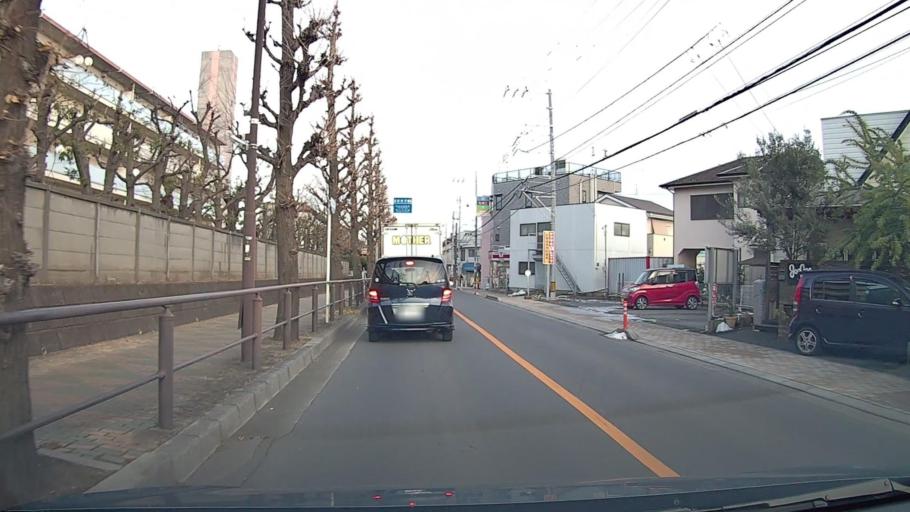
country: JP
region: Saitama
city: Wako
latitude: 35.7725
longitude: 139.6075
